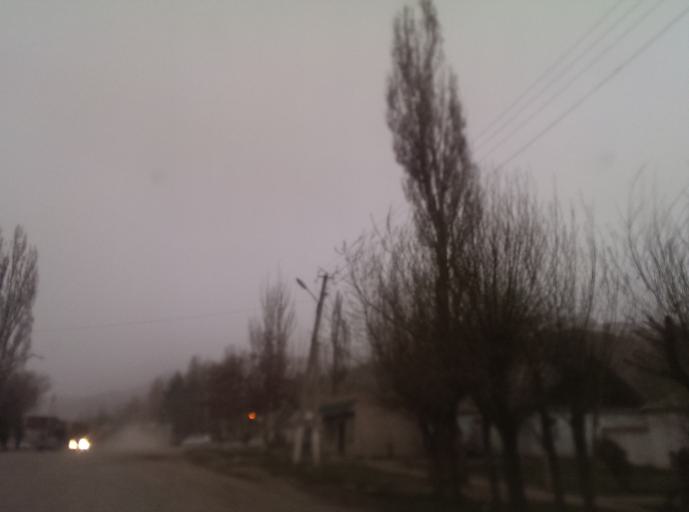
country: KG
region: Naryn
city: Naryn
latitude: 41.4233
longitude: 76.0171
